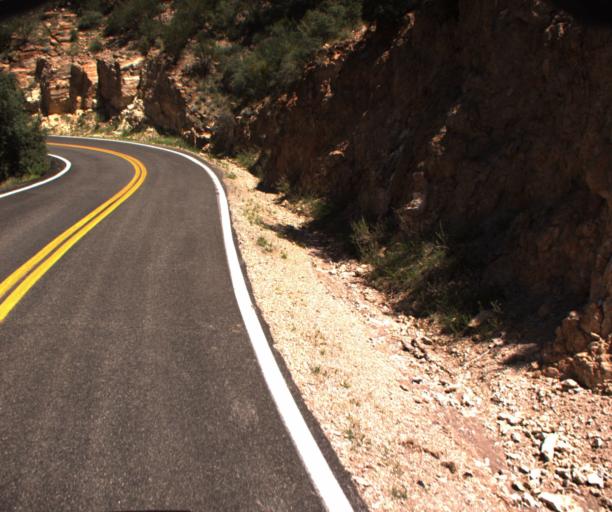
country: US
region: Arizona
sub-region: Greenlee County
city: Morenci
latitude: 33.1644
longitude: -109.3673
